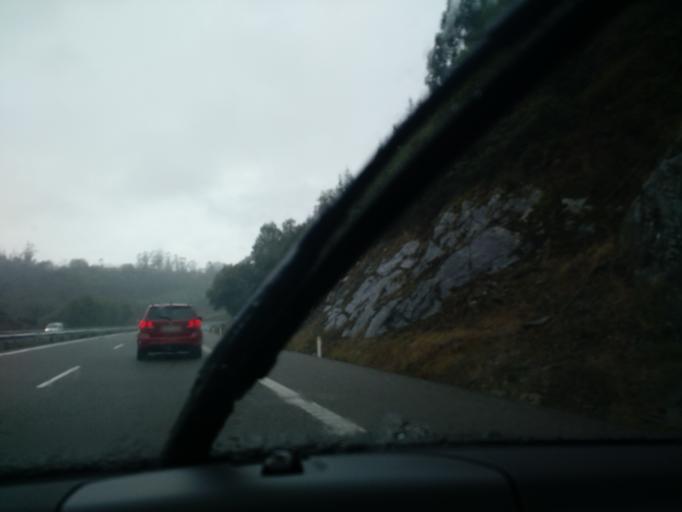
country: ES
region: Galicia
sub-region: Provincia da Coruna
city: Abegondo
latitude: 43.1637
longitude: -8.3258
